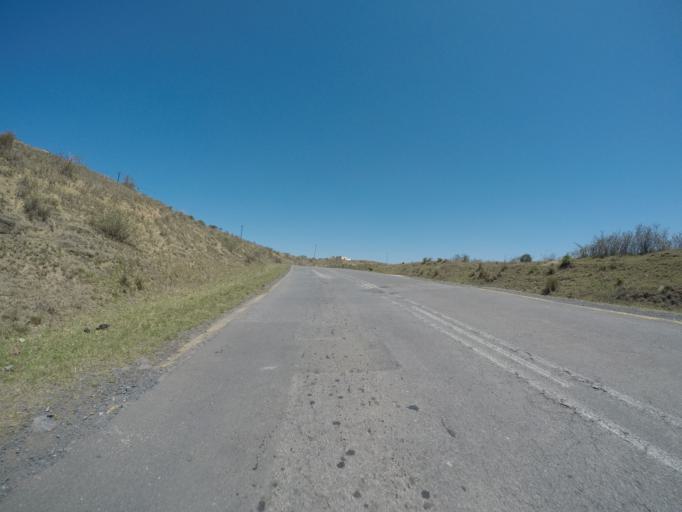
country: ZA
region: Eastern Cape
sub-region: OR Tambo District Municipality
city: Mthatha
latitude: -31.9108
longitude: 28.9575
